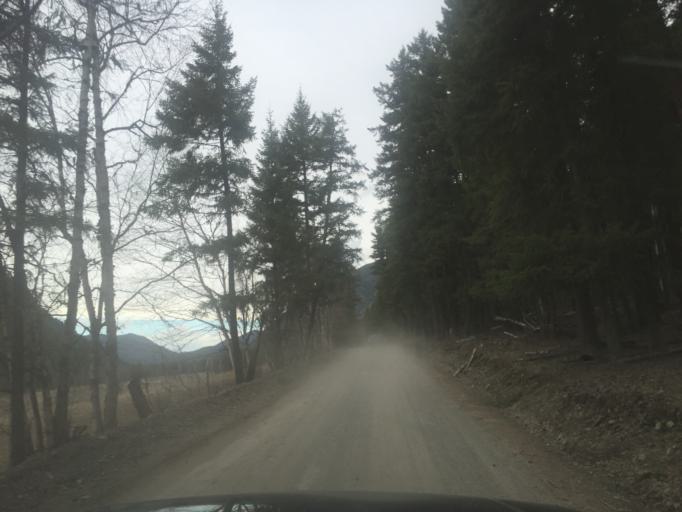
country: CA
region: British Columbia
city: Chase
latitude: 51.3926
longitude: -120.1265
